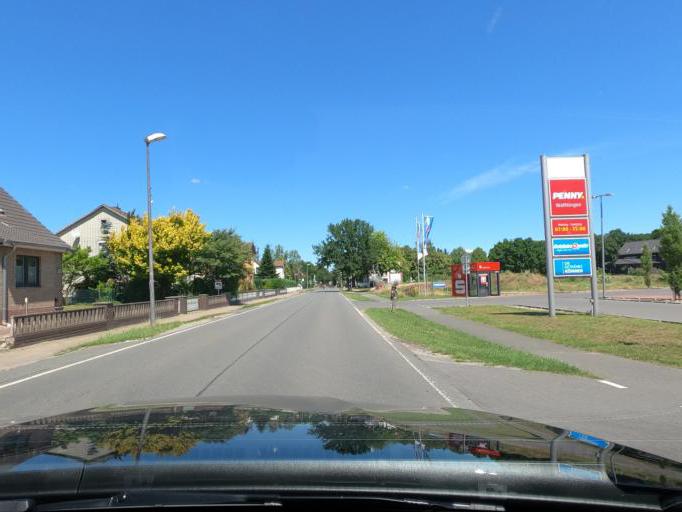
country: DE
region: Lower Saxony
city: Wathlingen
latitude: 52.5357
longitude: 10.1446
